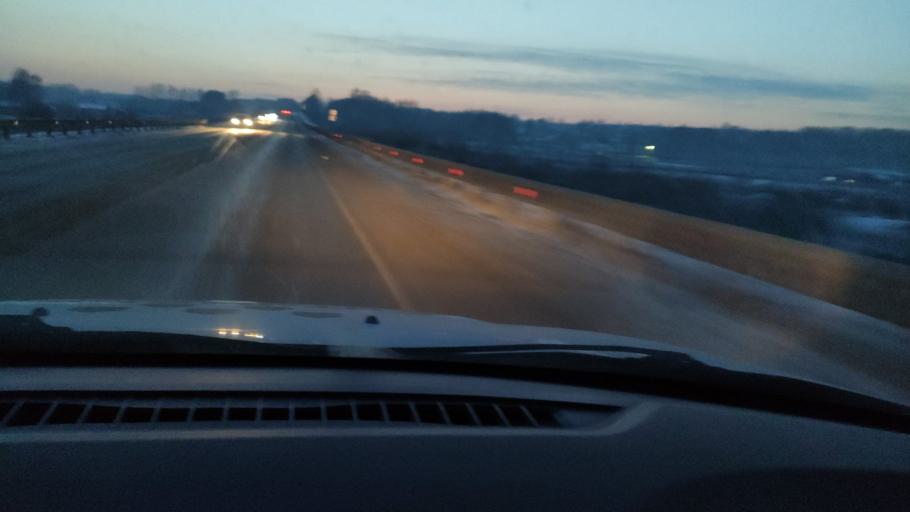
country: RU
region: Perm
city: Kungur
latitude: 57.4242
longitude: 56.9290
